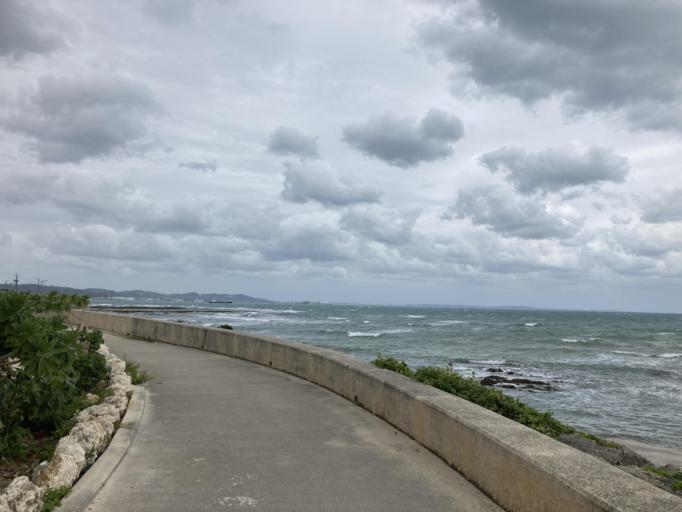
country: JP
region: Okinawa
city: Ginowan
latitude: 26.1839
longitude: 127.7784
